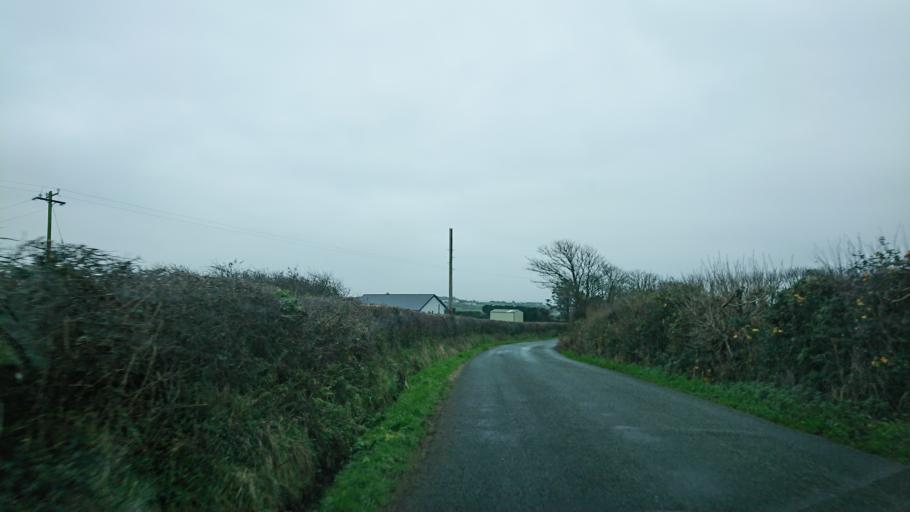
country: IE
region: Munster
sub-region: Waterford
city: Dunmore East
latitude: 52.1507
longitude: -7.0587
